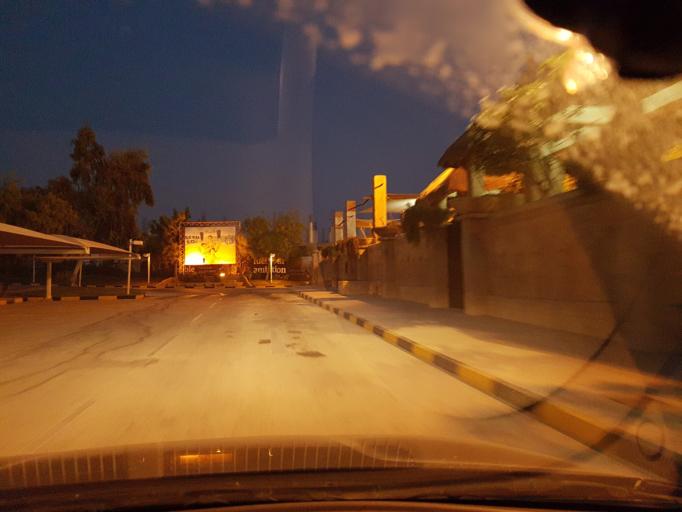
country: BH
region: Central Governorate
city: Dar Kulayb
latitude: 26.0148
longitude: 50.5103
